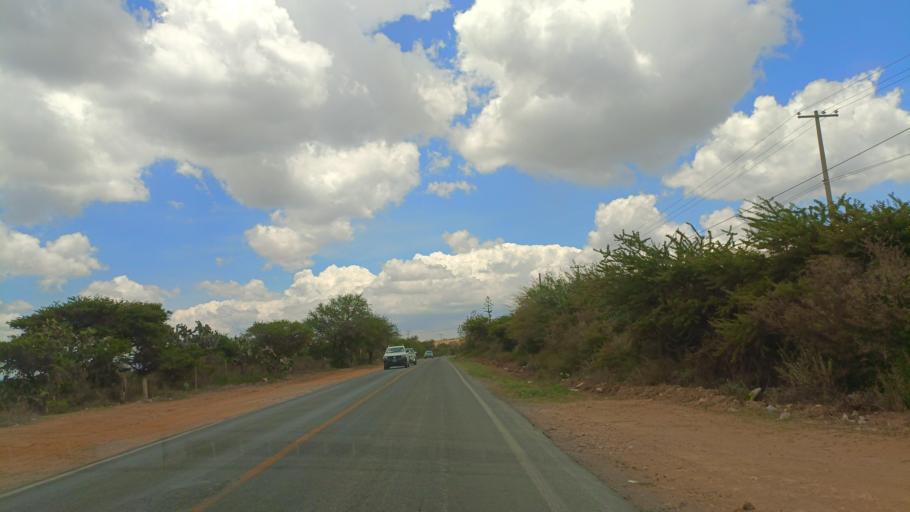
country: MX
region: Guanajuato
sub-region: San Luis de la Paz
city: San Ignacio
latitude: 21.2387
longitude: -100.4916
